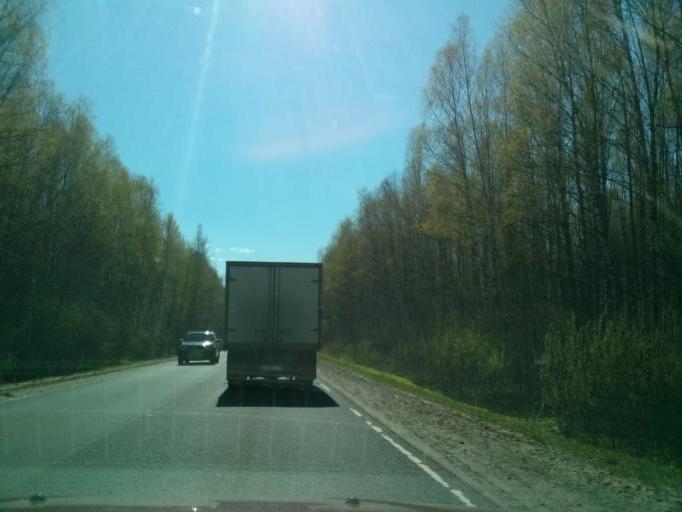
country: RU
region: Nizjnij Novgorod
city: Vorsma
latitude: 56.0188
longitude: 43.3493
